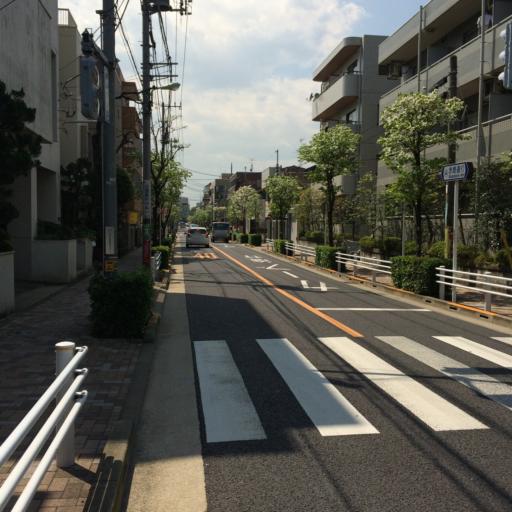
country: JP
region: Tokyo
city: Tokyo
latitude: 35.6570
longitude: 139.6556
